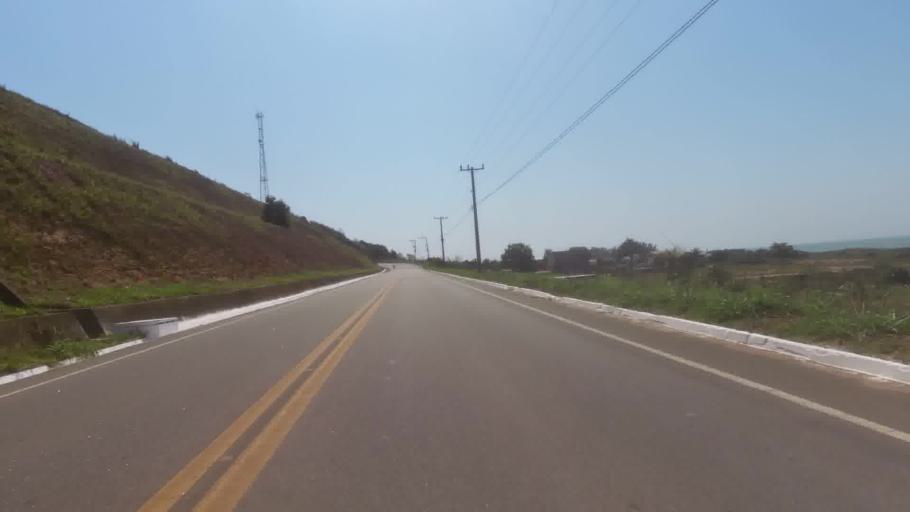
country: BR
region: Espirito Santo
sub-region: Marataizes
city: Marataizes
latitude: -21.0952
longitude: -40.8475
